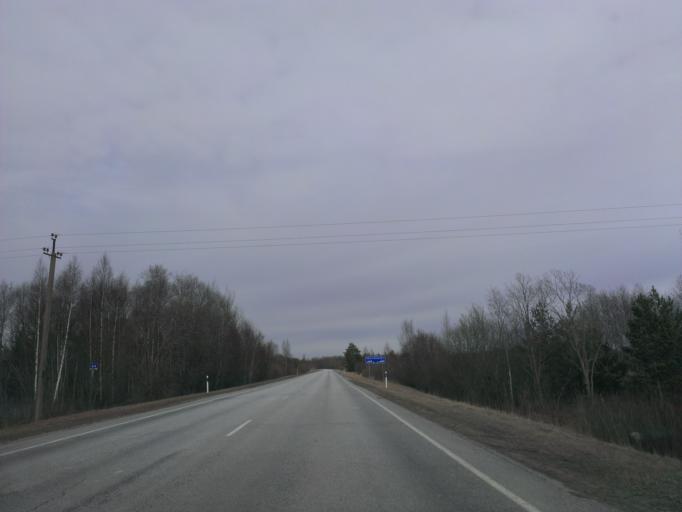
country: EE
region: Laeaene
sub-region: Lihula vald
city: Lihula
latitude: 58.5937
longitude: 23.5432
